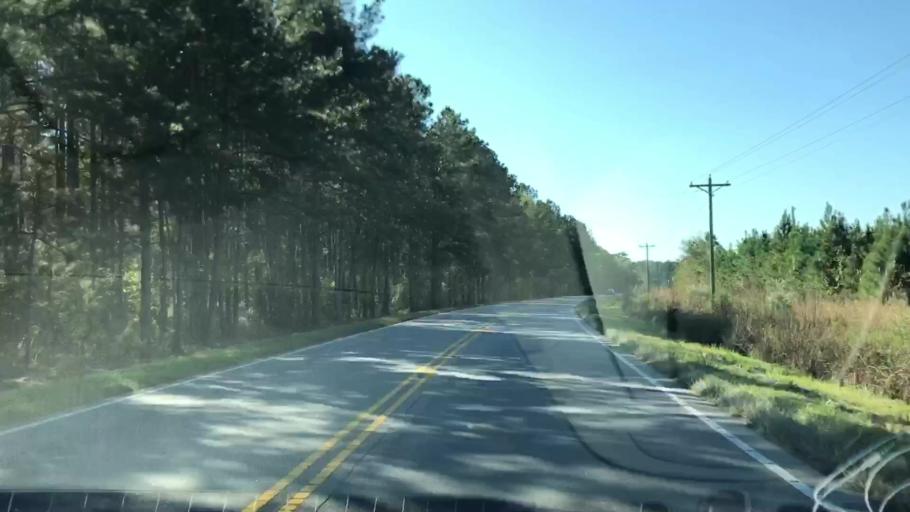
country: US
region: South Carolina
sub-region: Jasper County
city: Ridgeland
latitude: 32.4131
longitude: -80.9009
